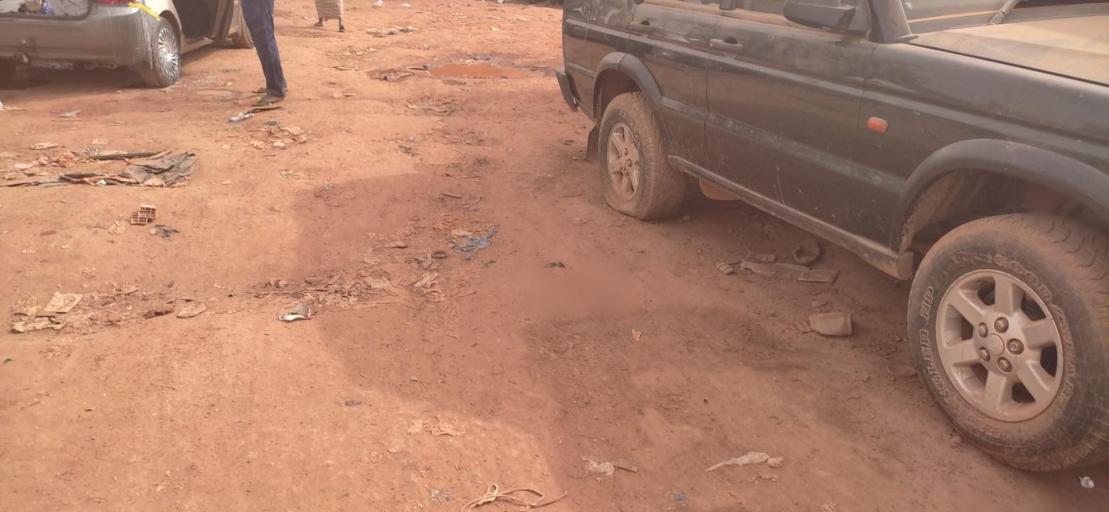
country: BF
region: Centre
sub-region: Kadiogo Province
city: Ouagadougou
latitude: 12.3419
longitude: -1.5339
